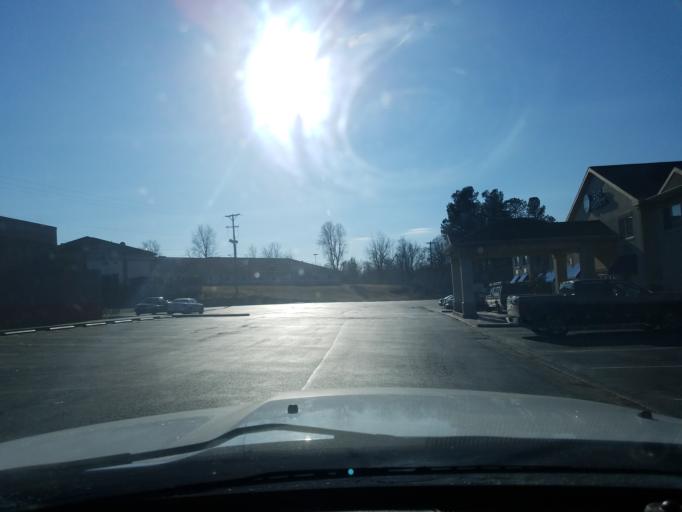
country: US
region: Kentucky
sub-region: Muhlenberg County
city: Central City
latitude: 37.2864
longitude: -87.1163
